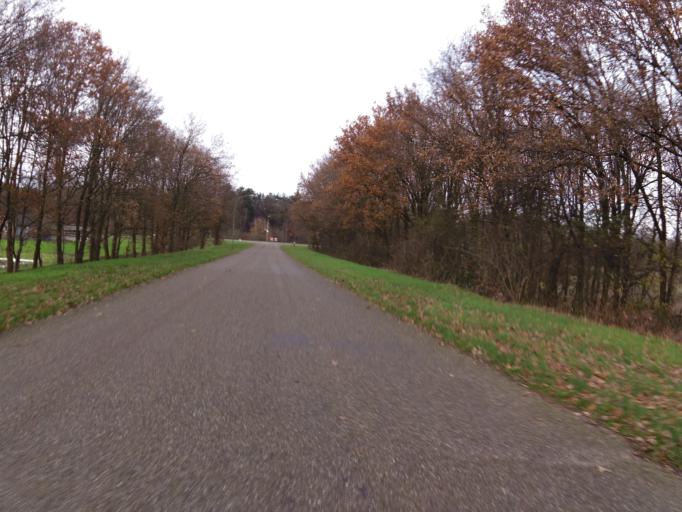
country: NL
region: North Brabant
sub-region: Gemeente Oss
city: Berghem
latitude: 51.7456
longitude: 5.5907
